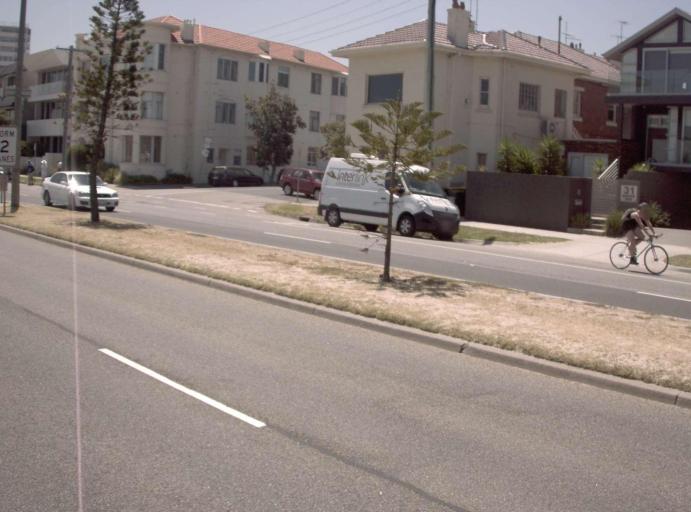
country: AU
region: Victoria
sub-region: Port Phillip
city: Saint Kilda
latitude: -37.8724
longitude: 144.9764
